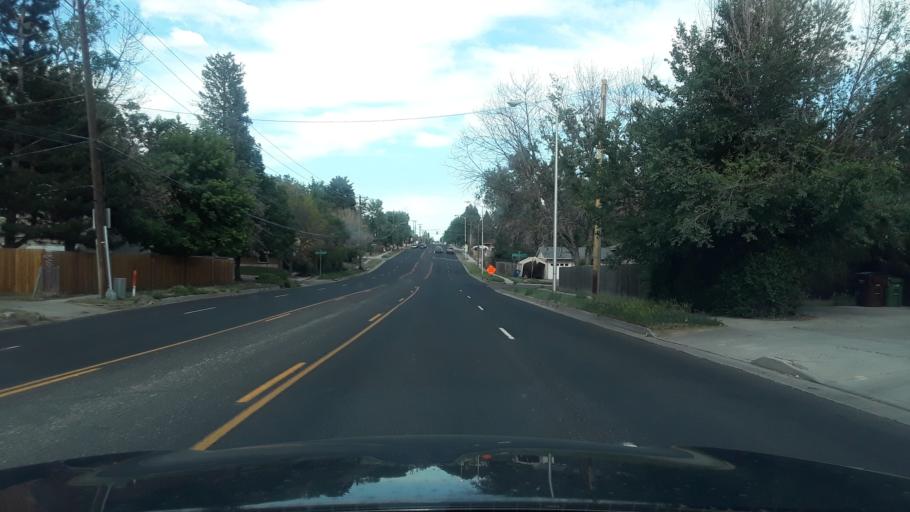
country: US
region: Colorado
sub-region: El Paso County
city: Colorado Springs
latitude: 38.8471
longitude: -104.7695
